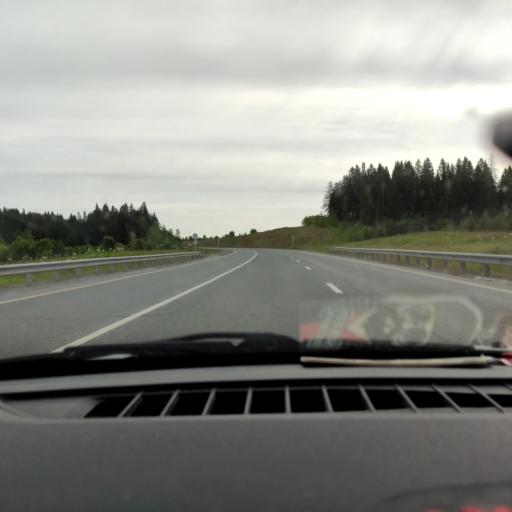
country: RU
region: Perm
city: Polazna
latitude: 58.2839
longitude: 56.4661
